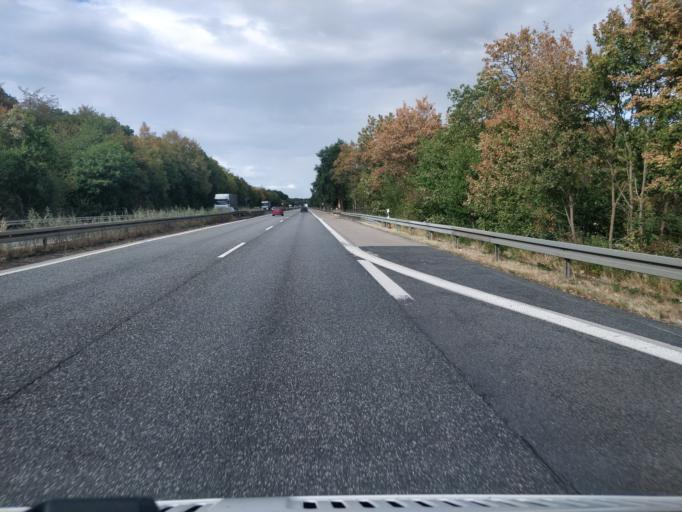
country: DE
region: North Rhine-Westphalia
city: Meckenheim
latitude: 50.6555
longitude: 7.0495
